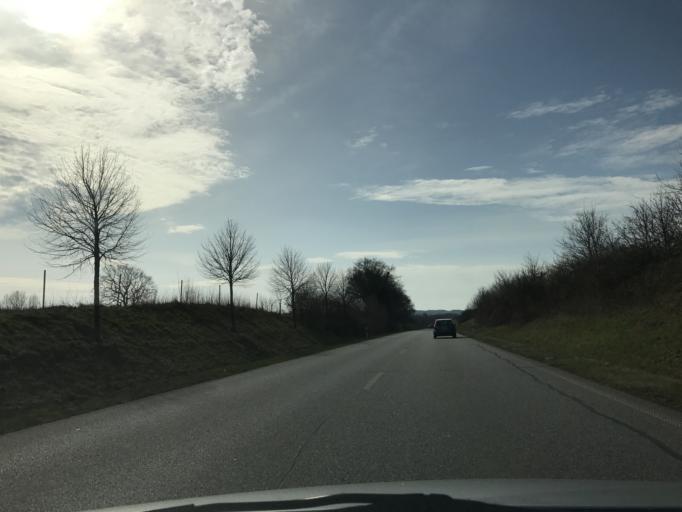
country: DE
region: Schleswig-Holstein
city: Klein Wittensee
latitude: 54.3994
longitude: 9.7444
